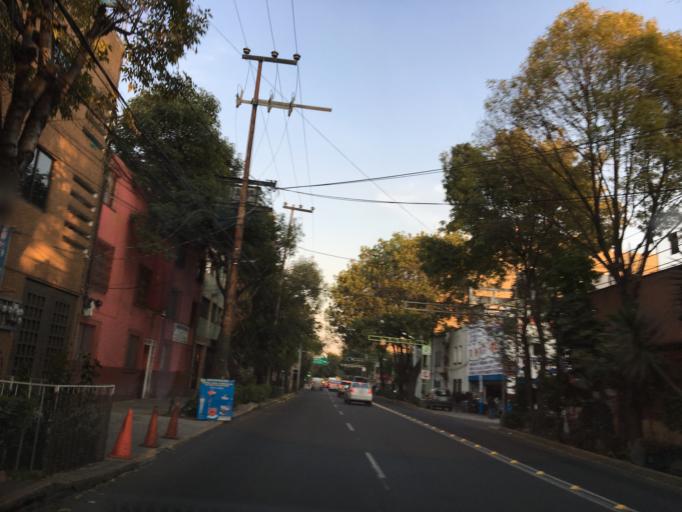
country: MX
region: Mexico City
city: Benito Juarez
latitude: 19.4148
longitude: -99.1498
